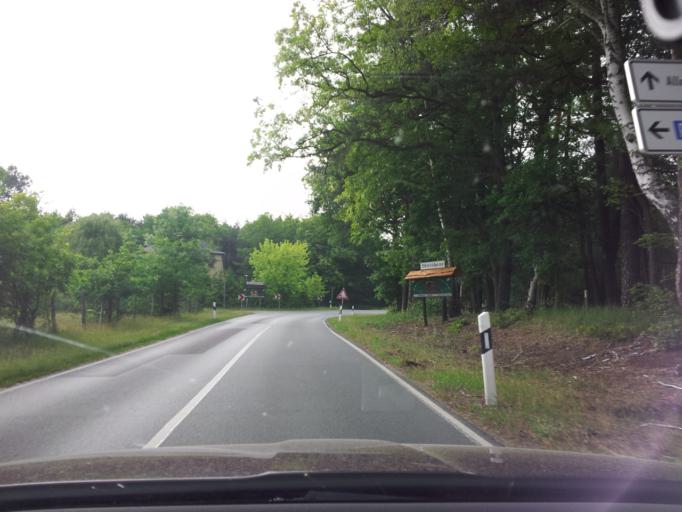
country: DE
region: Brandenburg
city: Fichtenwalde
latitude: 52.3026
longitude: 12.9309
